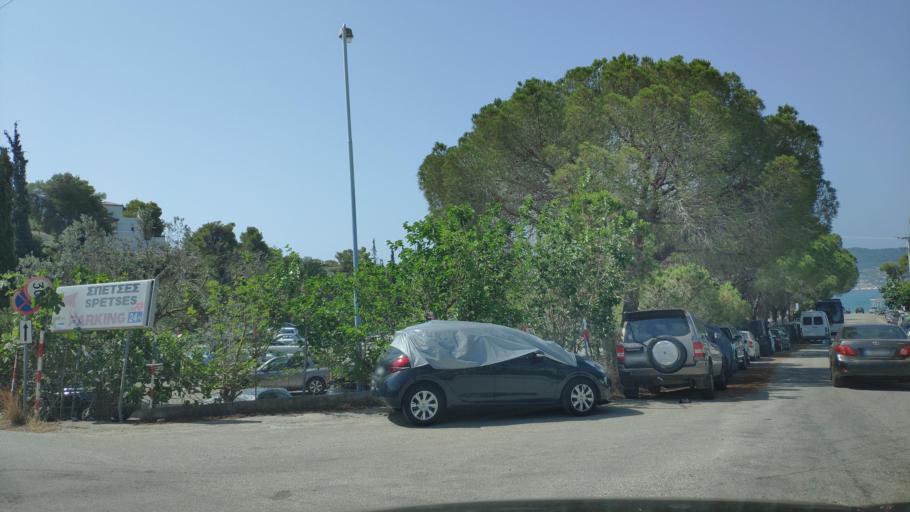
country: GR
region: Attica
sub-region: Nomos Piraios
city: Spetses
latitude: 37.2973
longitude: 23.1642
